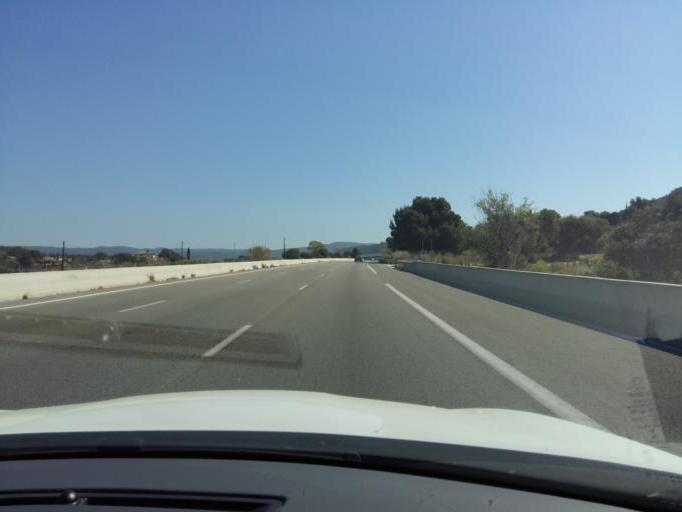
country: FR
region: Provence-Alpes-Cote d'Azur
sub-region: Departement du Var
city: Saint-Cyr-sur-Mer
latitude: 43.2025
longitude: 5.7316
